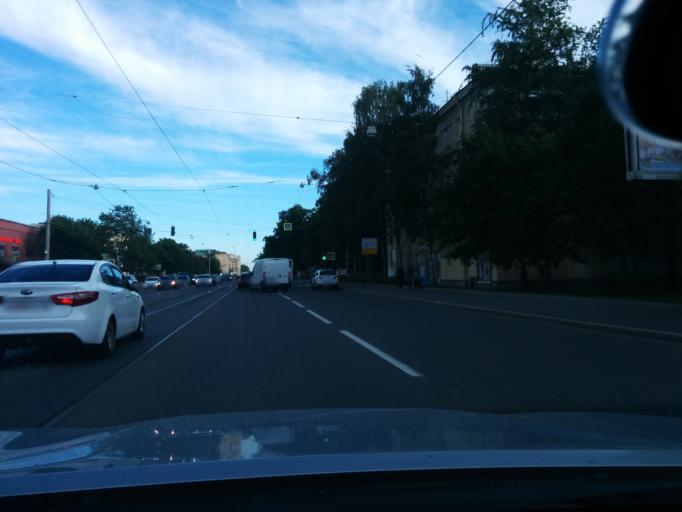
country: RU
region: Leningrad
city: Svetlanovskiy
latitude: 60.0095
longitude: 30.3252
